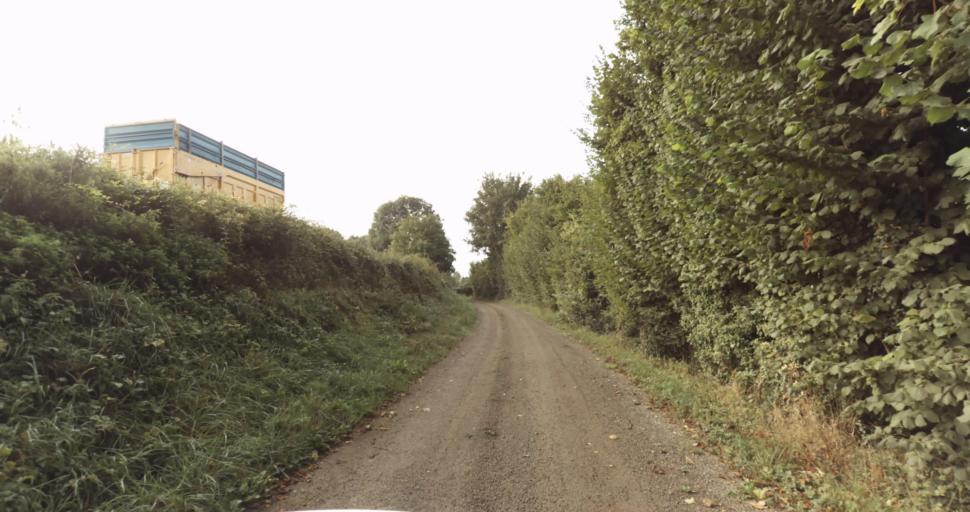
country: FR
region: Lower Normandy
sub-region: Departement de l'Orne
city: Vimoutiers
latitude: 48.9092
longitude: 0.2708
